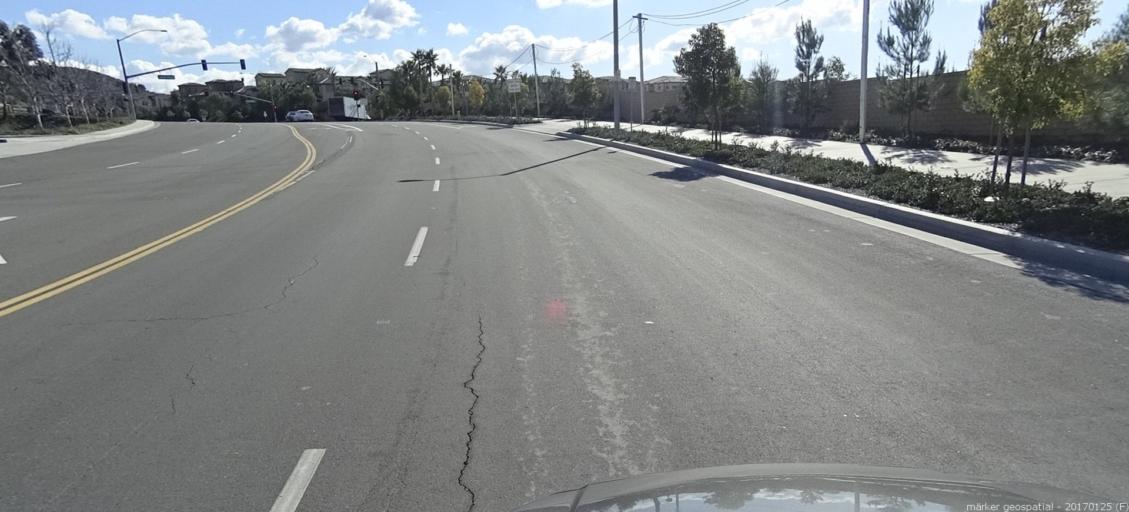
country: US
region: California
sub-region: Orange County
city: Foothill Ranch
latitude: 33.6791
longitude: -117.6784
